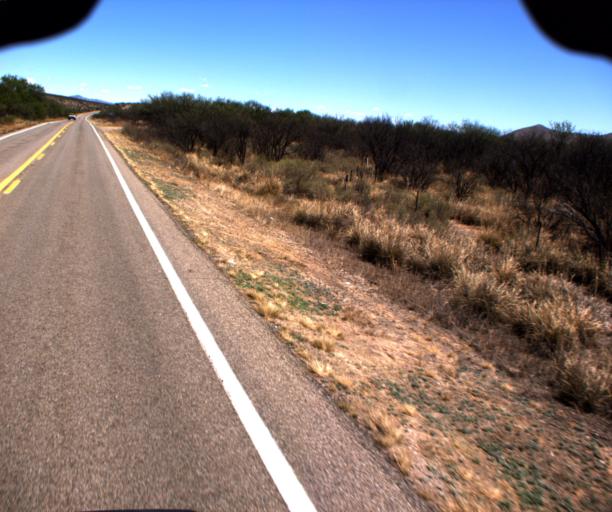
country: US
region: Arizona
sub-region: Cochise County
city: Tombstone
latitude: 31.7239
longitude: -110.1844
